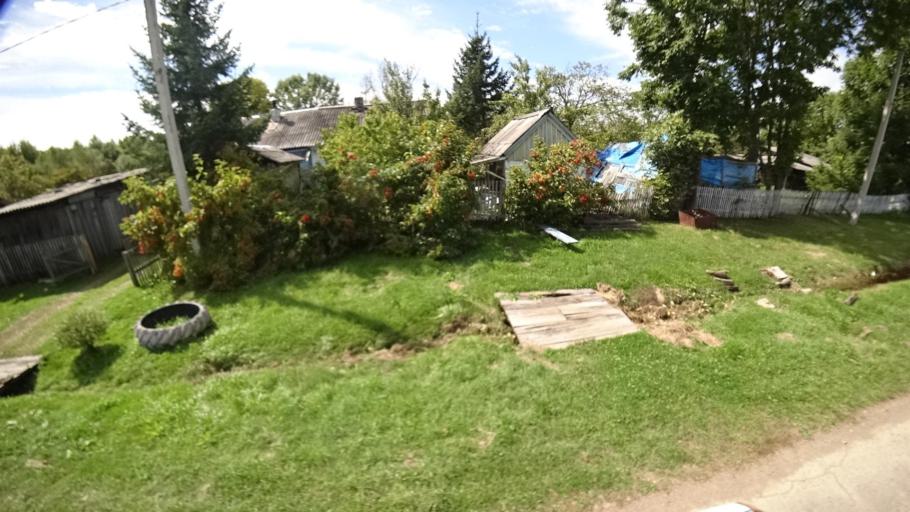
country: RU
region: Primorskiy
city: Yakovlevka
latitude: 44.7087
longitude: 133.6376
